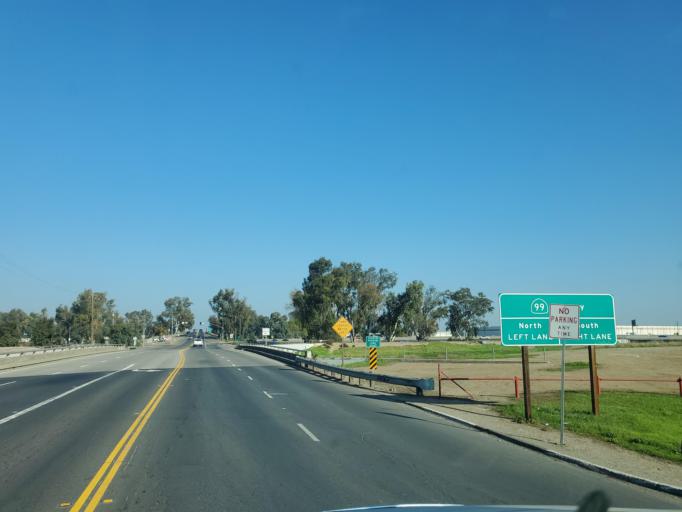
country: US
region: California
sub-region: San Joaquin County
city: August
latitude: 37.9826
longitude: -121.2532
